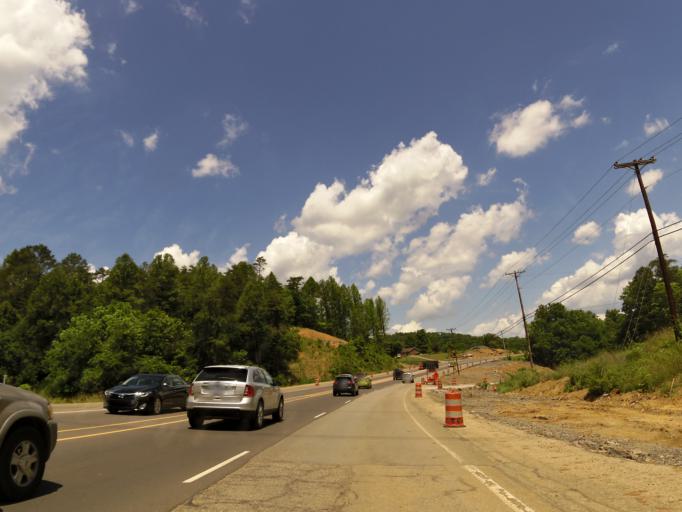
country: US
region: Tennessee
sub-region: Union County
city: Condon
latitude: 36.1550
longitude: -83.9145
